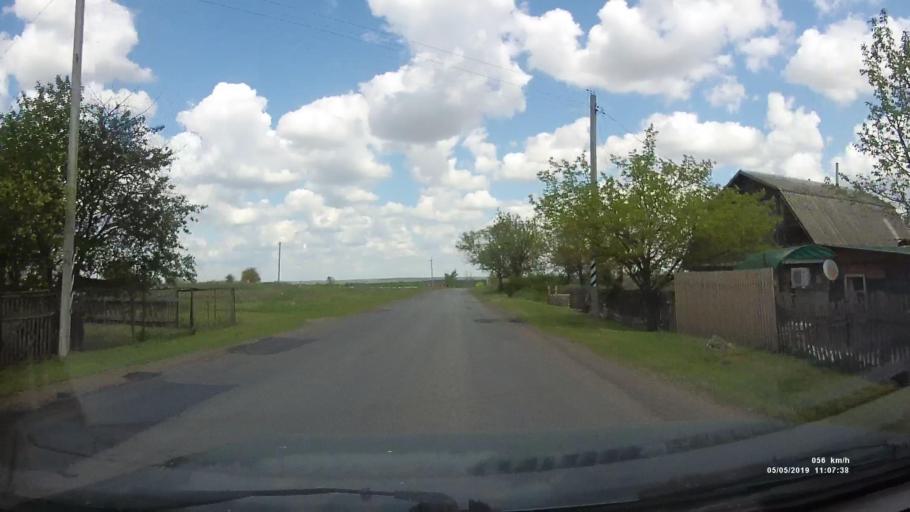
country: RU
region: Rostov
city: Ust'-Donetskiy
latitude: 47.7270
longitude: 40.9141
